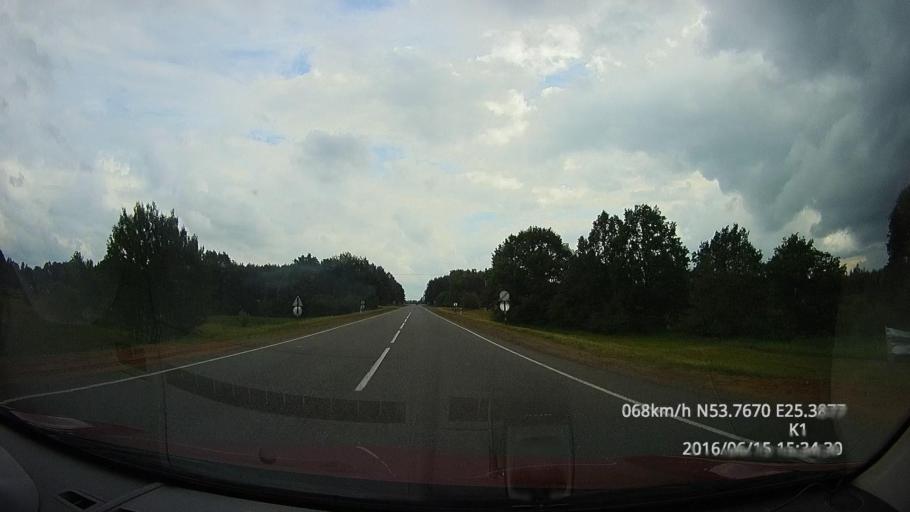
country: BY
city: Berezovka
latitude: 53.7664
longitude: 25.3880
